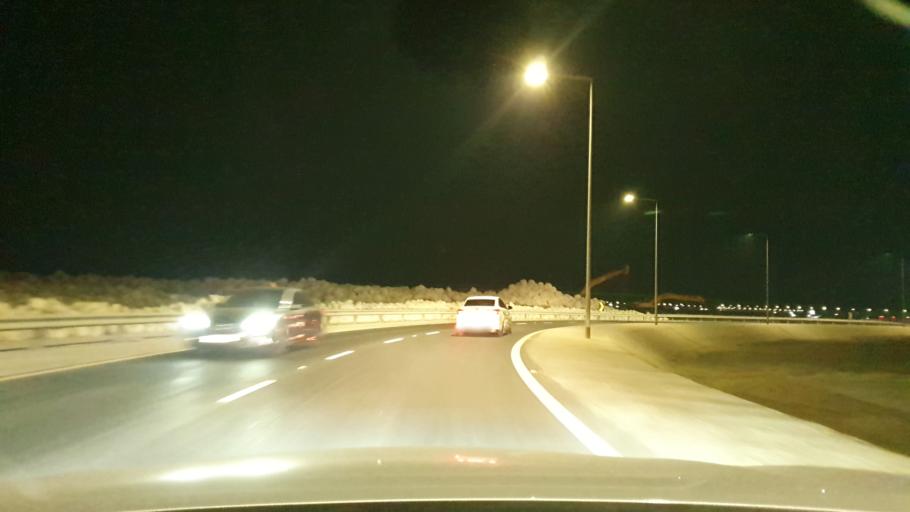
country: BH
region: Muharraq
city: Al Muharraq
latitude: 26.2732
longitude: 50.5921
